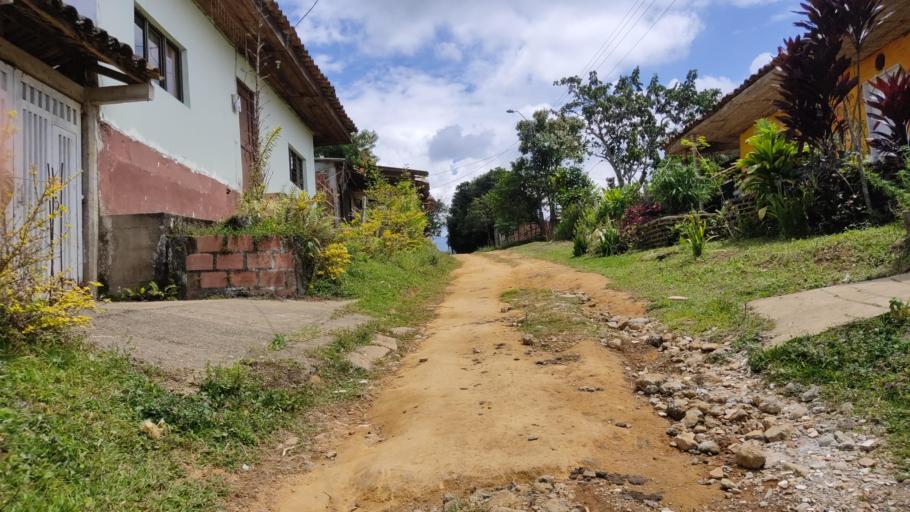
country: CO
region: Valle del Cauca
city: Jamundi
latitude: 3.2100
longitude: -76.6523
